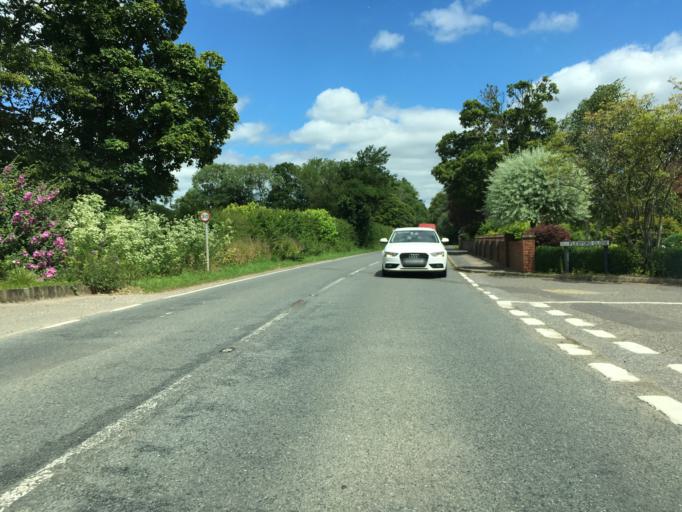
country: GB
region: England
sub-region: Hampshire
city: Highclere
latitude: 51.3385
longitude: -1.3756
